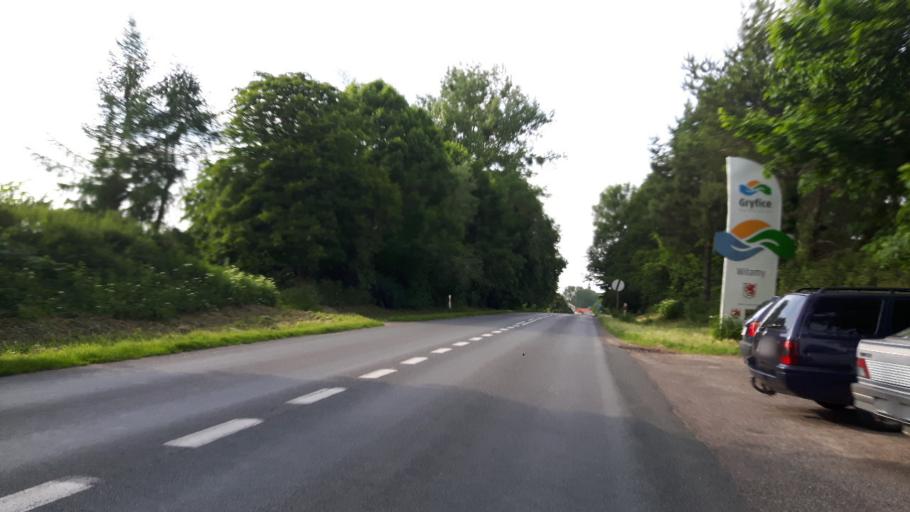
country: PL
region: West Pomeranian Voivodeship
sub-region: Powiat gryficki
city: Gryfice
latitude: 53.9019
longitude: 15.2031
